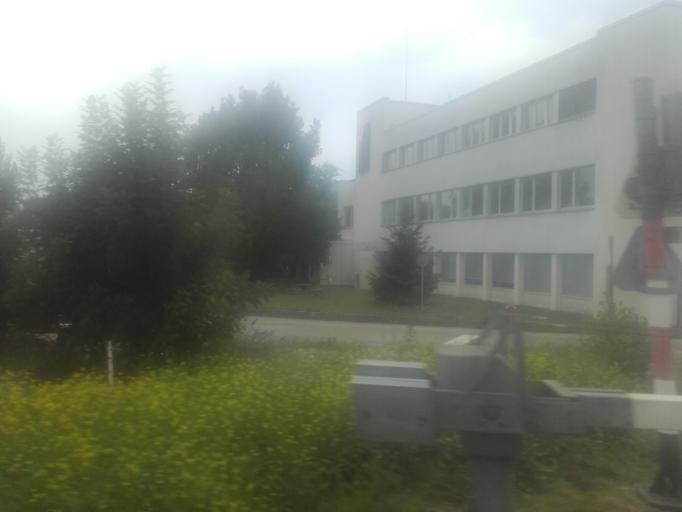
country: CH
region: Bern
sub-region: Emmental District
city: Burgdorf
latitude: 47.0658
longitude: 7.6076
